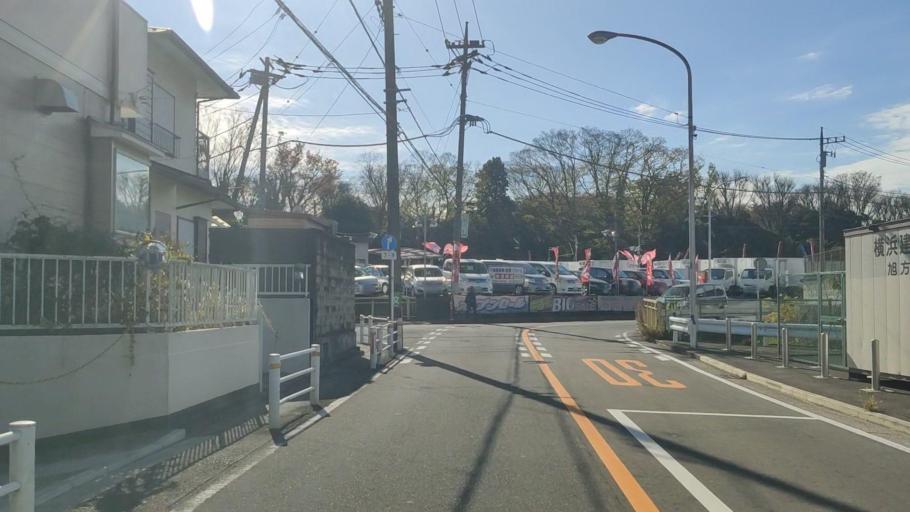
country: JP
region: Kanagawa
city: Minami-rinkan
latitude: 35.4553
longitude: 139.5389
